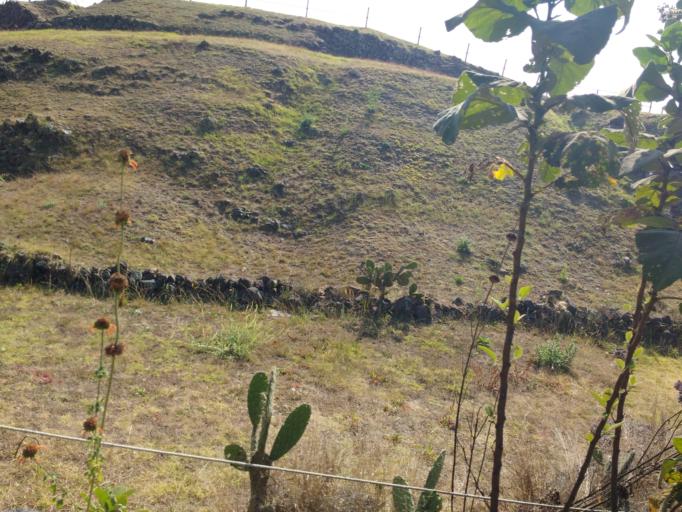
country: MX
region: Mexico City
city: Tlalpan
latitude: 19.3023
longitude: -99.1818
